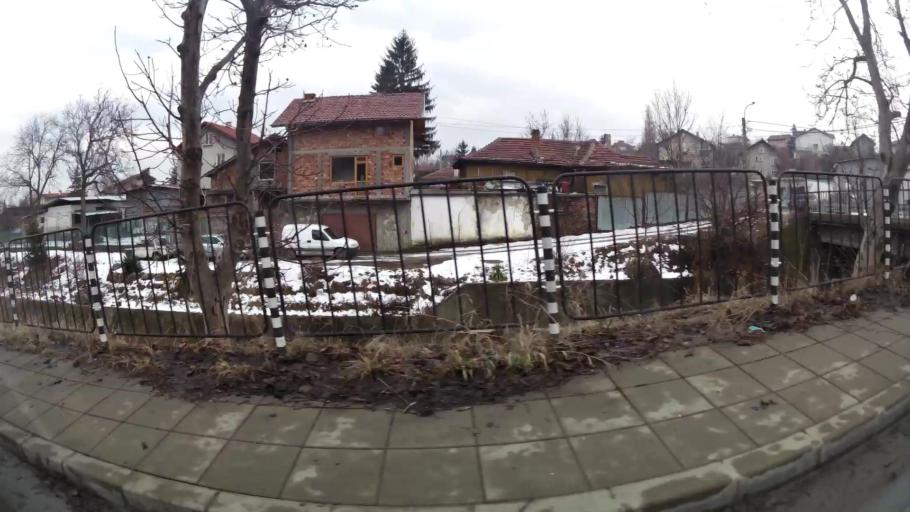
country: BG
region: Sofiya
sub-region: Obshtina Bozhurishte
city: Bozhurishte
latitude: 42.6975
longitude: 23.2215
